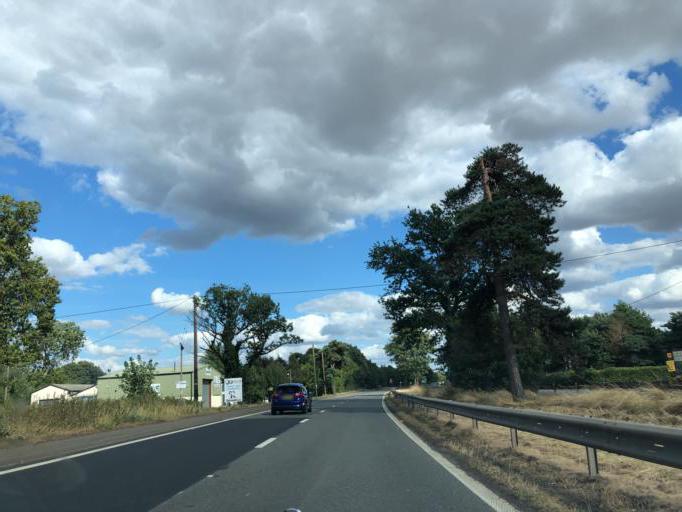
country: GB
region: England
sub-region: Warwickshire
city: Dunchurch
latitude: 52.3428
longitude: -1.3291
